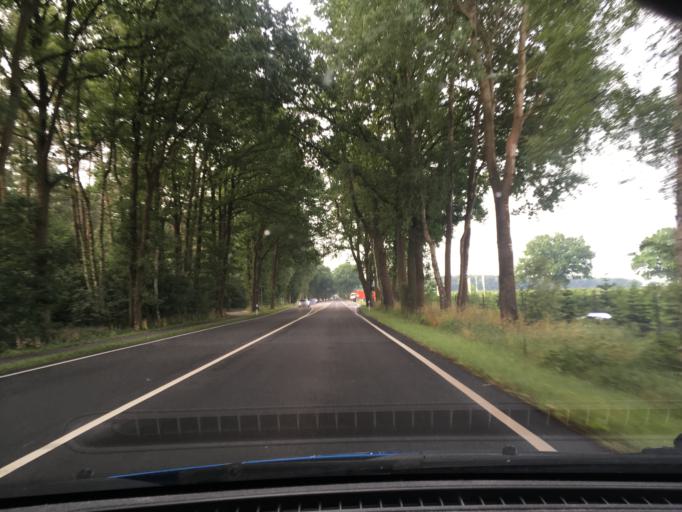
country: DE
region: Lower Saxony
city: Wenzendorf
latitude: 53.3479
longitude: 9.8095
